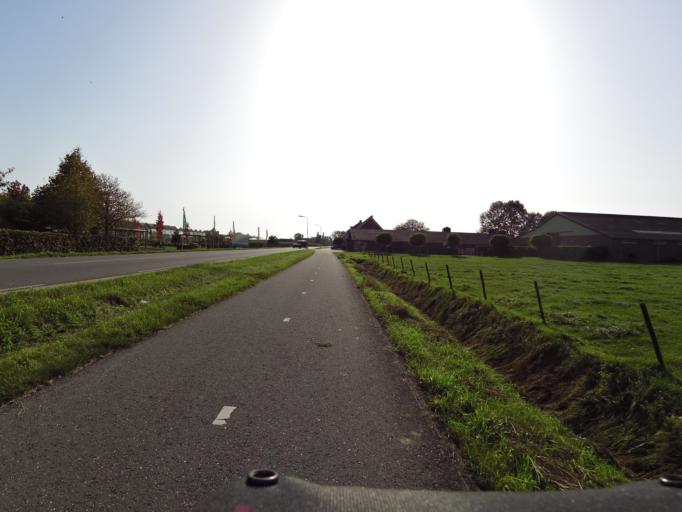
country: NL
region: Gelderland
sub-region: Gemeente Westervoort
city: Westervoort
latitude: 51.8915
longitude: 5.9794
